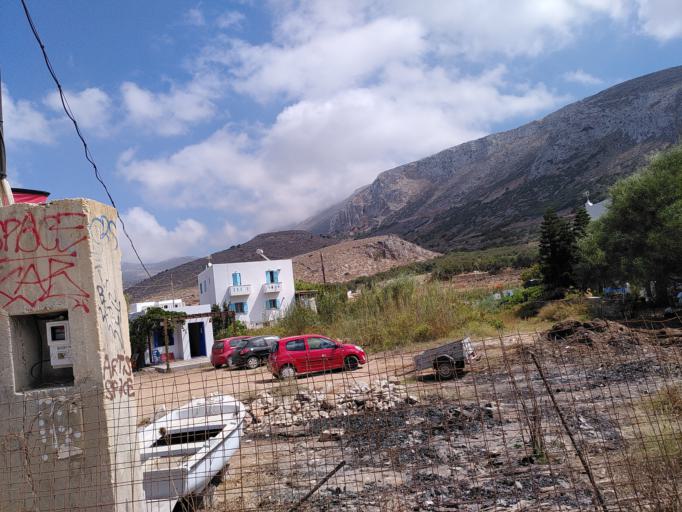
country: GR
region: South Aegean
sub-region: Nomos Kykladon
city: Amorgos
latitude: 36.9025
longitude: 25.9780
